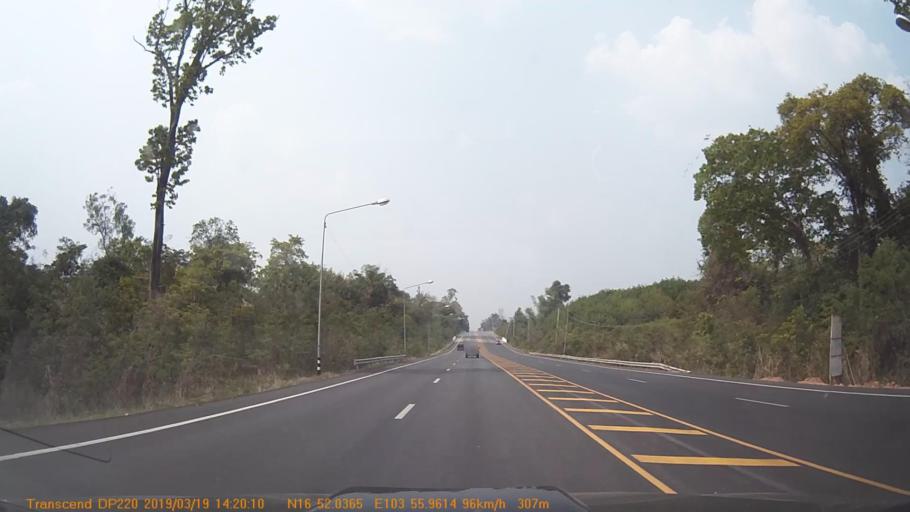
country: TH
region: Sakon Nakhon
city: Phu Phan
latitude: 16.8678
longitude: 103.9326
